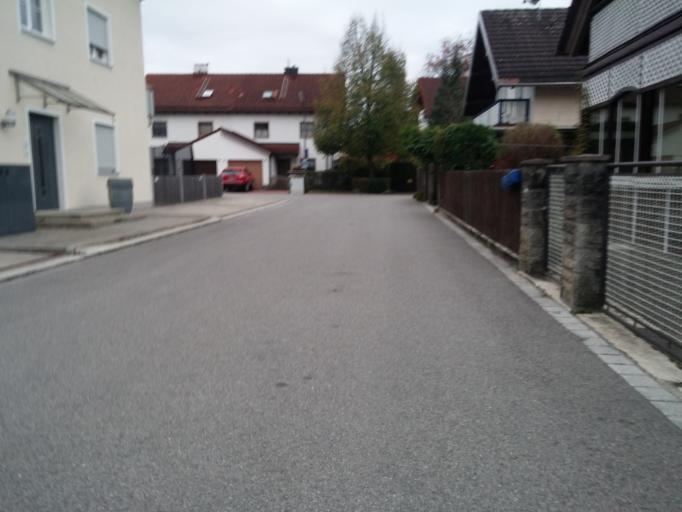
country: DE
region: Bavaria
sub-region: Upper Bavaria
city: Kirchseeon
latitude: 48.0736
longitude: 11.8890
